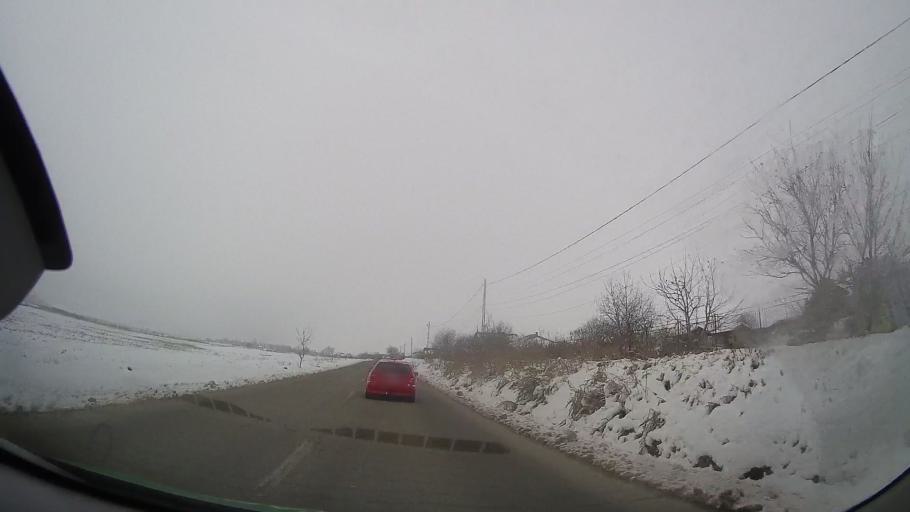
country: RO
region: Vaslui
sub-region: Comuna Negresti
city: Negresti
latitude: 46.8381
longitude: 27.4379
